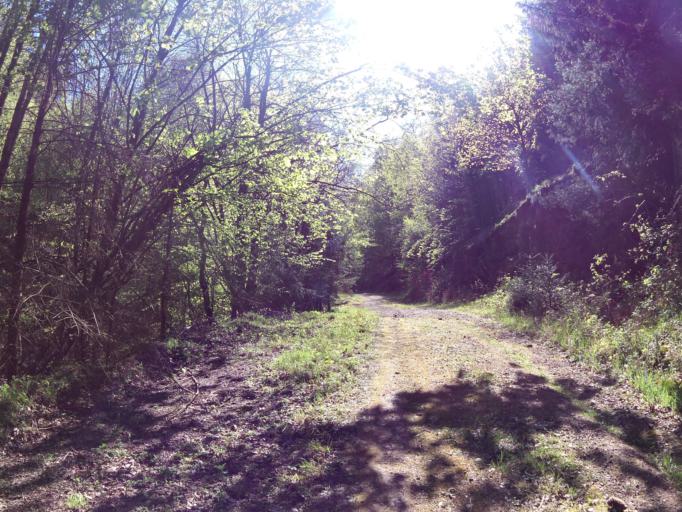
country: DE
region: Thuringia
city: Wolfsburg-Unkeroda
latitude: 50.9693
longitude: 10.2551
